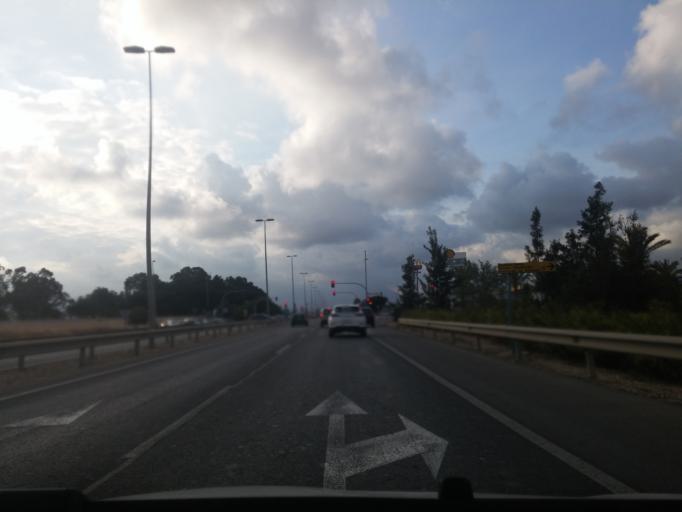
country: ES
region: Valencia
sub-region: Provincia de Alicante
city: San Vicent del Raspeig
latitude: 38.3728
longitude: -0.5063
